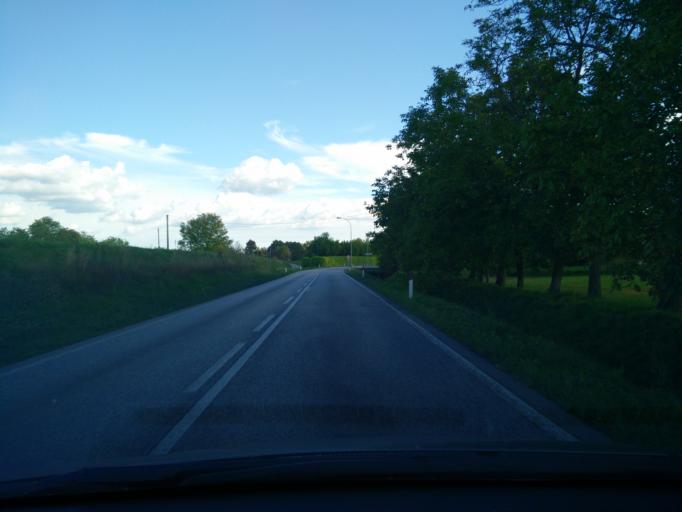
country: IT
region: Veneto
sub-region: Provincia di Treviso
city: Breda
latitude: 45.7432
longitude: 12.3464
